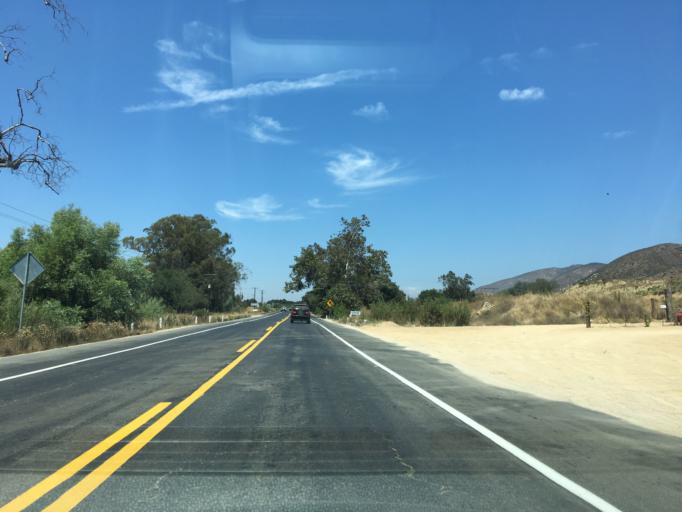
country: MX
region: Baja California
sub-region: Ensenada
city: Rancho Verde
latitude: 31.9990
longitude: -116.6369
